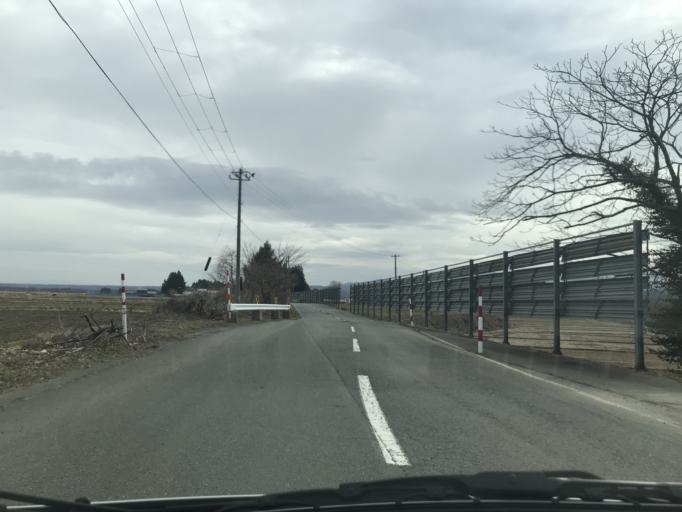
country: JP
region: Iwate
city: Hanamaki
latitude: 39.3430
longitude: 140.9821
